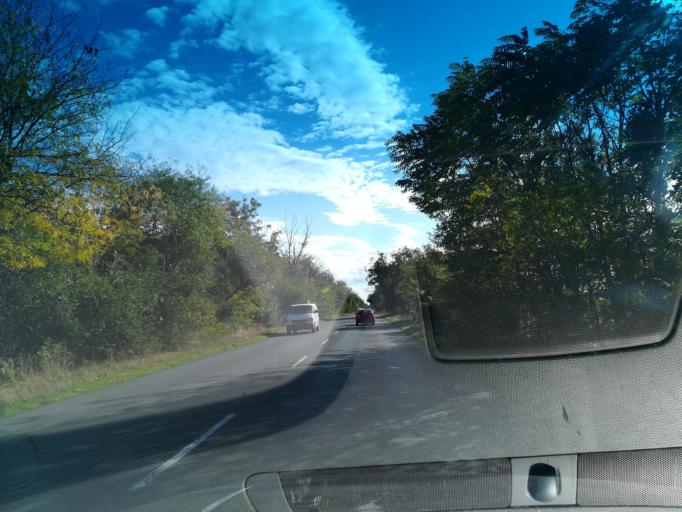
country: BG
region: Stara Zagora
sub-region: Obshtina Stara Zagora
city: Stara Zagora
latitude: 42.3715
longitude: 25.6528
